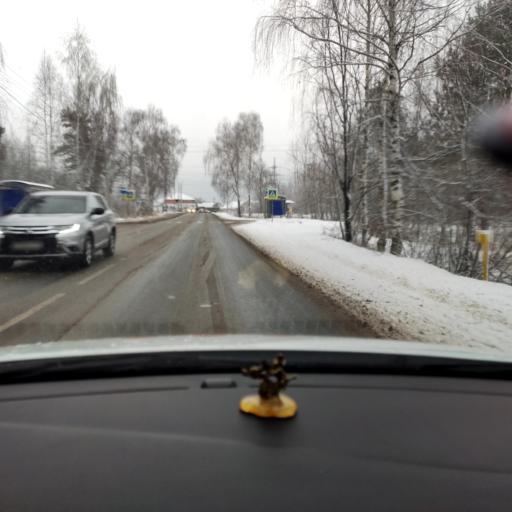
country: RU
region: Tatarstan
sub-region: Zelenodol'skiy Rayon
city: Zelenodolsk
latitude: 55.8663
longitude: 48.5387
